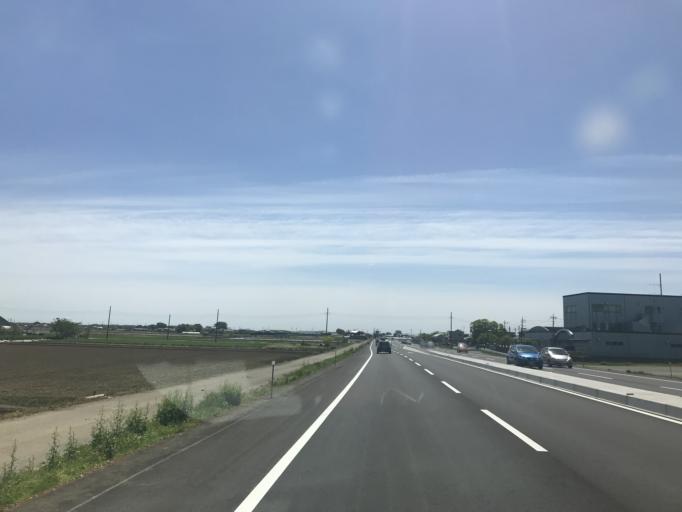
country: JP
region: Ibaraki
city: Shimodate
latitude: 36.2266
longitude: 139.9857
